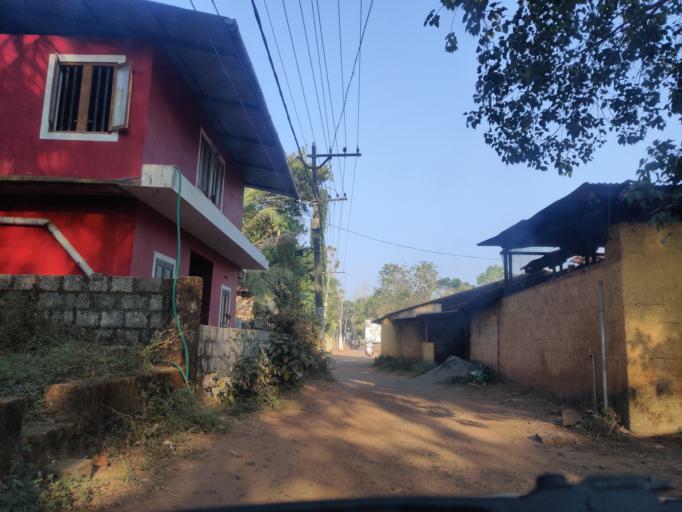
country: IN
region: Kerala
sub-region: Malappuram
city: Ponnani
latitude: 10.7282
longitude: 76.0072
